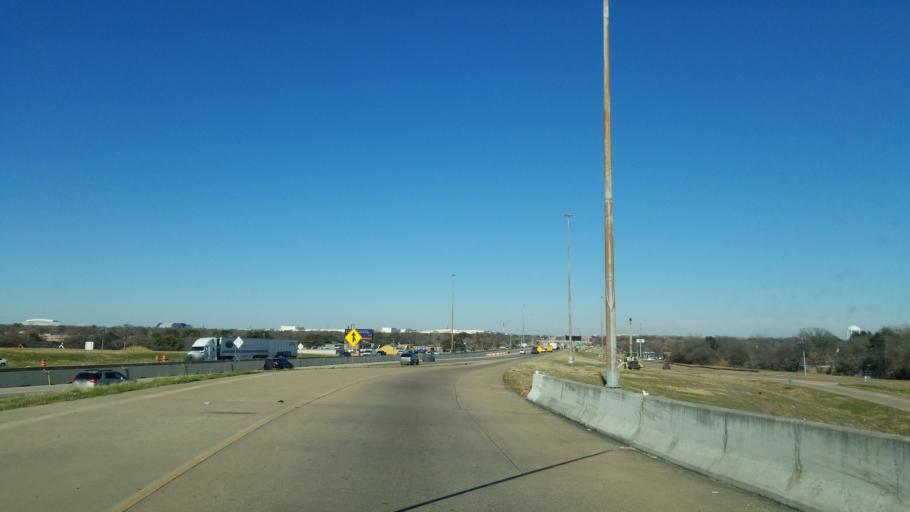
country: US
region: Texas
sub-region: Tarrant County
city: Arlington
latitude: 32.7162
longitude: -97.0623
